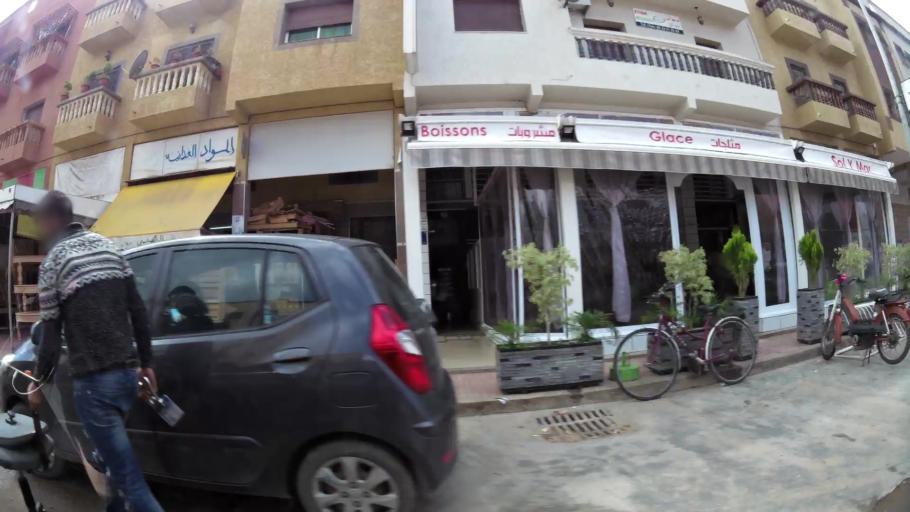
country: MA
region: Grand Casablanca
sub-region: Mediouna
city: Mediouna
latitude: 33.3756
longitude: -7.5358
